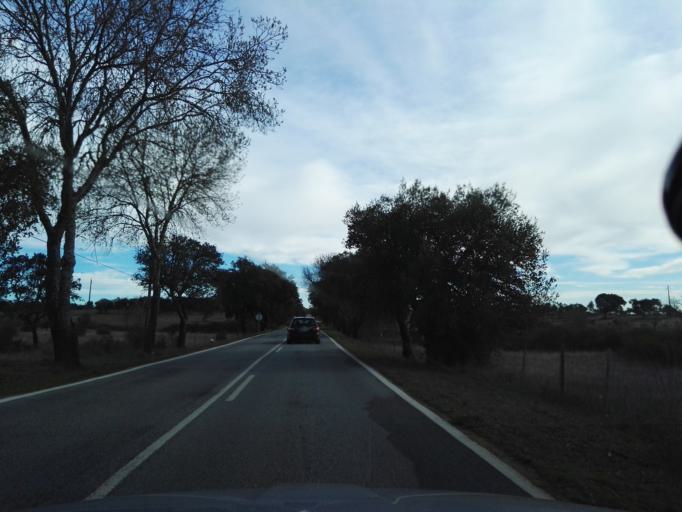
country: PT
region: Portalegre
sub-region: Nisa
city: Nisa
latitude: 39.4914
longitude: -7.7169
